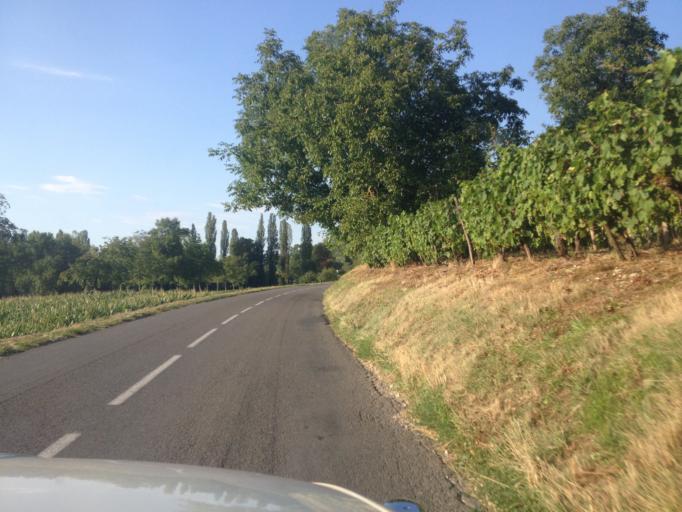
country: FR
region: Rhone-Alpes
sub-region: Departement de la Savoie
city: Mery
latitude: 45.6497
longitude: 5.9362
